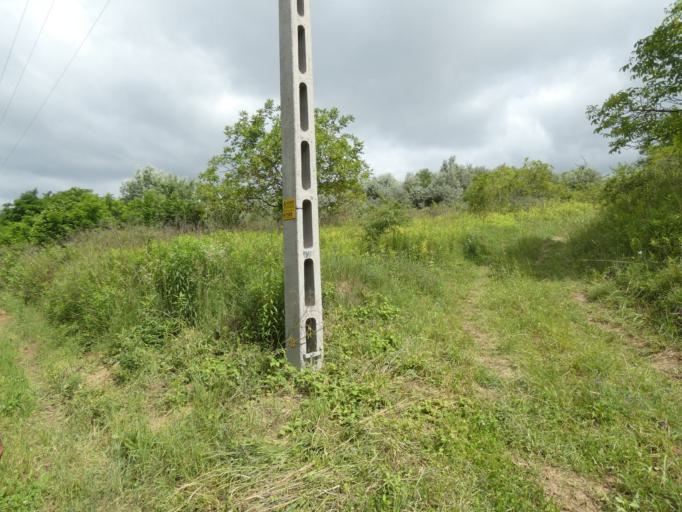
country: HU
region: Pest
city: Mende
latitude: 47.4092
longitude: 19.4781
